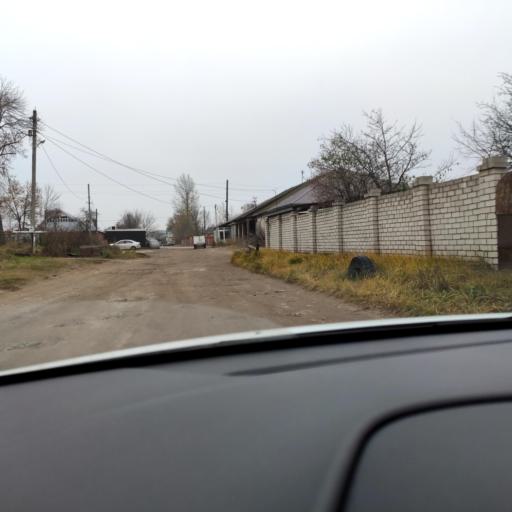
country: RU
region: Tatarstan
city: Vysokaya Gora
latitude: 55.8490
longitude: 49.2193
